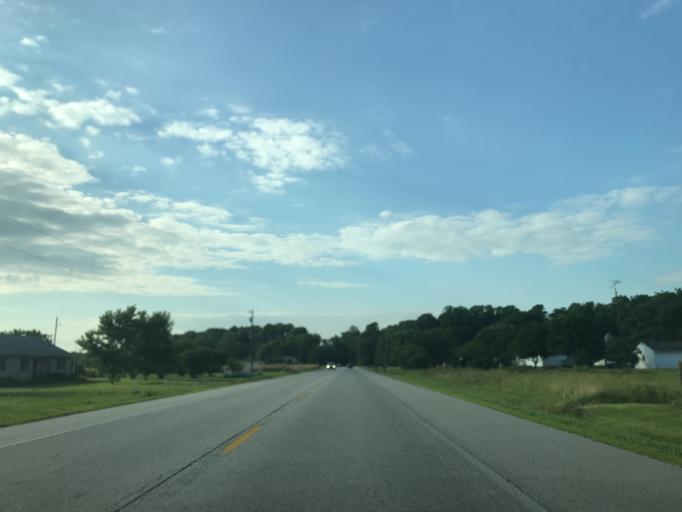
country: US
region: Maryland
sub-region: Caroline County
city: Federalsburg
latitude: 38.7266
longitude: -75.7862
